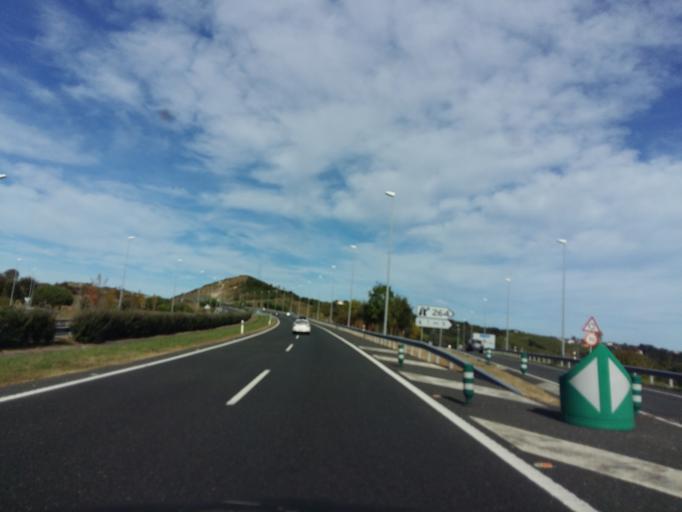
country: ES
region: Cantabria
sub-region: Provincia de Cantabria
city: San Vicente de la Barquera
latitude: 43.3650
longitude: -4.3983
